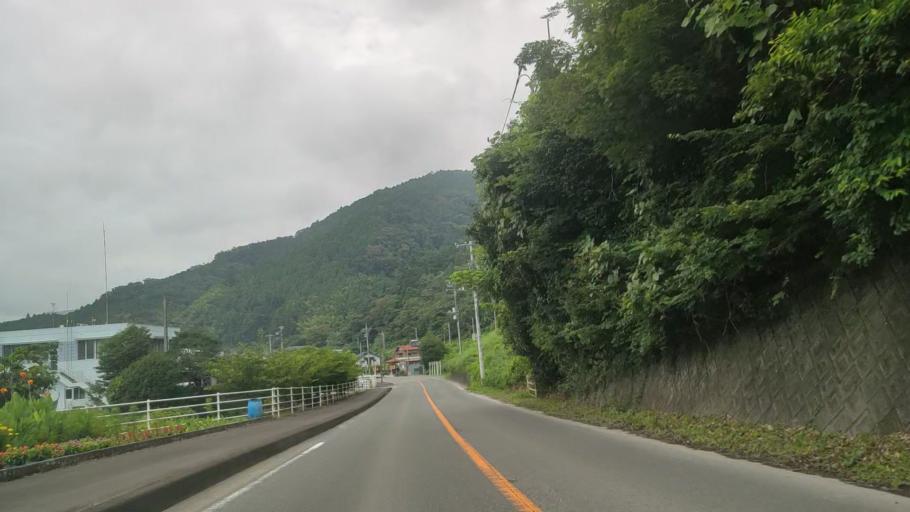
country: JP
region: Shizuoka
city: Fujinomiya
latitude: 35.2072
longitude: 138.5539
